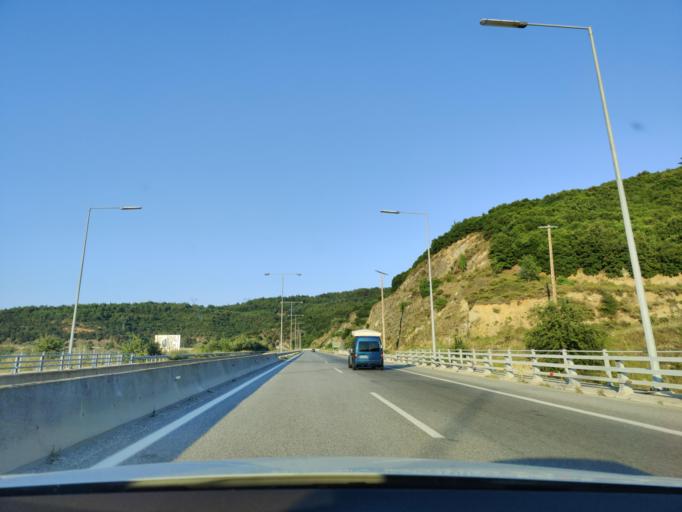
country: GR
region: East Macedonia and Thrace
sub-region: Nomos Kavalas
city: Kavala
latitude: 40.9550
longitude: 24.3862
